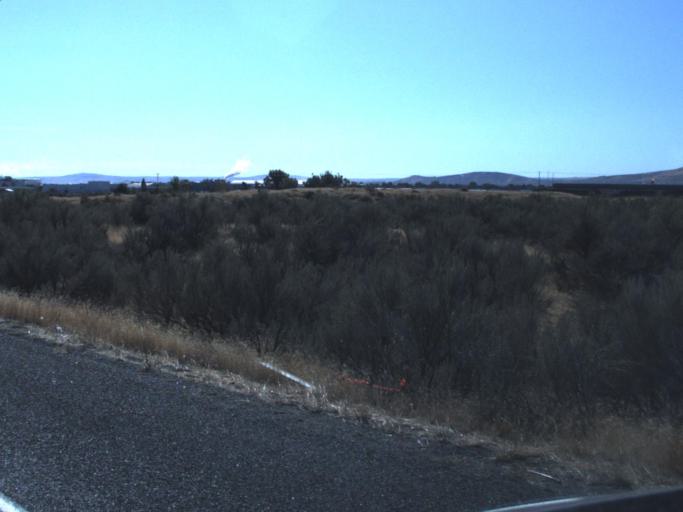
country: US
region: Washington
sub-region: Benton County
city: Richland
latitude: 46.3192
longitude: -119.3038
